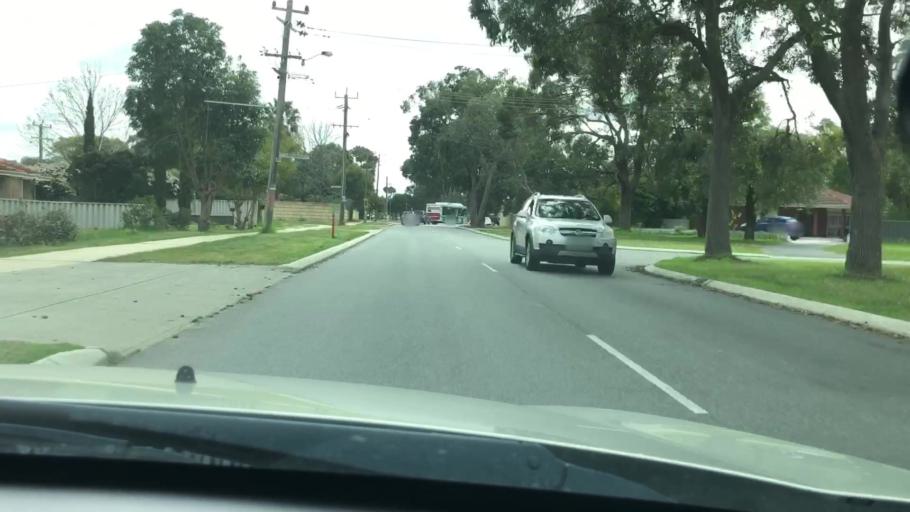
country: AU
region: Western Australia
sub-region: Armadale
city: Armadale
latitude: -32.1480
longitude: 115.9966
